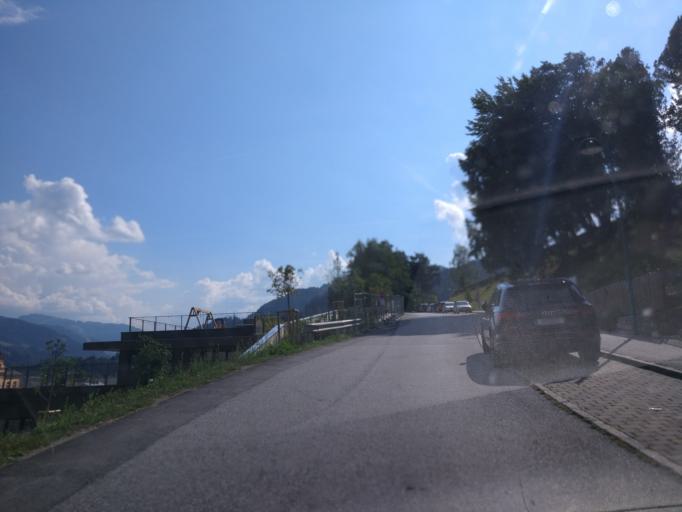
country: AT
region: Salzburg
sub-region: Politischer Bezirk Sankt Johann im Pongau
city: Bischofshofen
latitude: 47.4151
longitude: 13.2168
